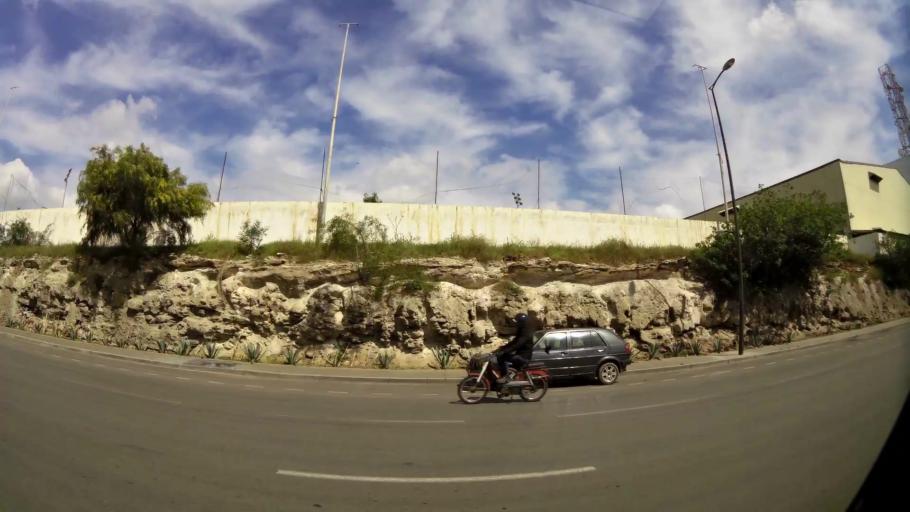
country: MA
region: Grand Casablanca
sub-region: Casablanca
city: Casablanca
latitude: 33.6025
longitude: -7.5530
